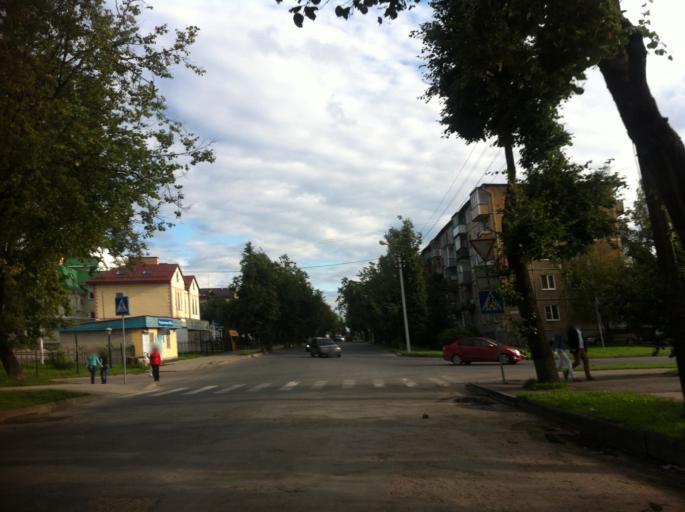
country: RU
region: Pskov
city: Pskov
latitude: 57.8218
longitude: 28.3201
